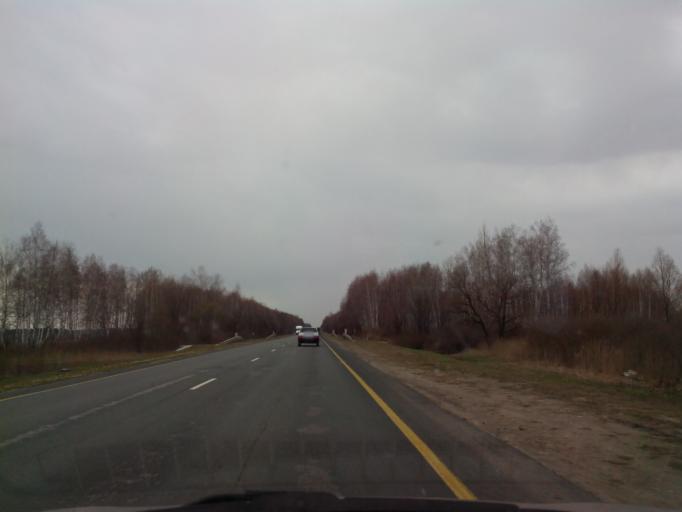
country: RU
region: Tambov
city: Michurinsk
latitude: 53.0597
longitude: 40.4522
